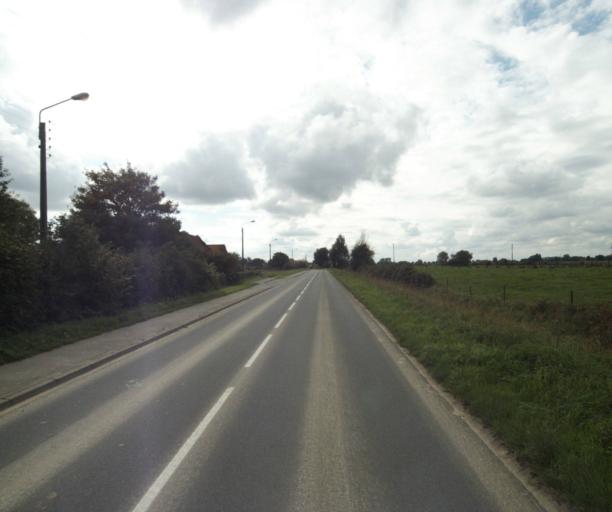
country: FR
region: Nord-Pas-de-Calais
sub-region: Departement du Nord
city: Premesques
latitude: 50.6678
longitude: 2.9440
